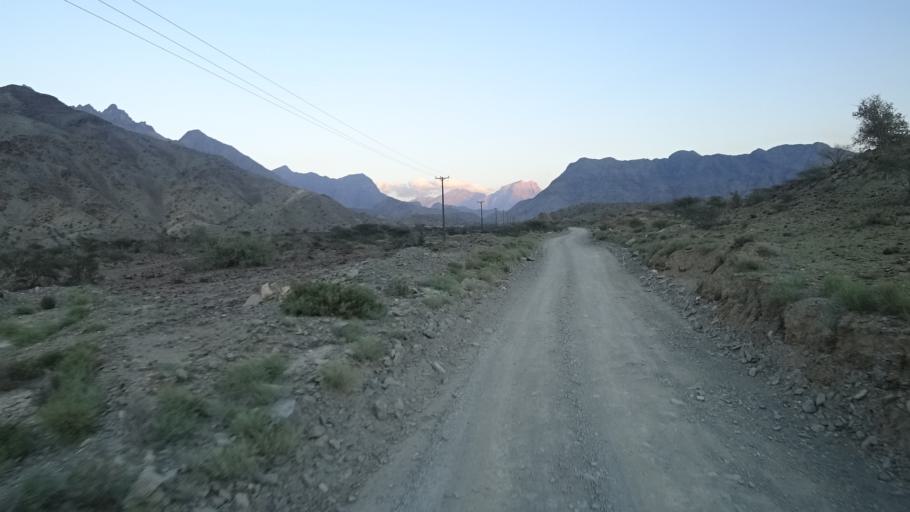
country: OM
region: Al Batinah
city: Rustaq
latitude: 23.2813
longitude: 57.3463
